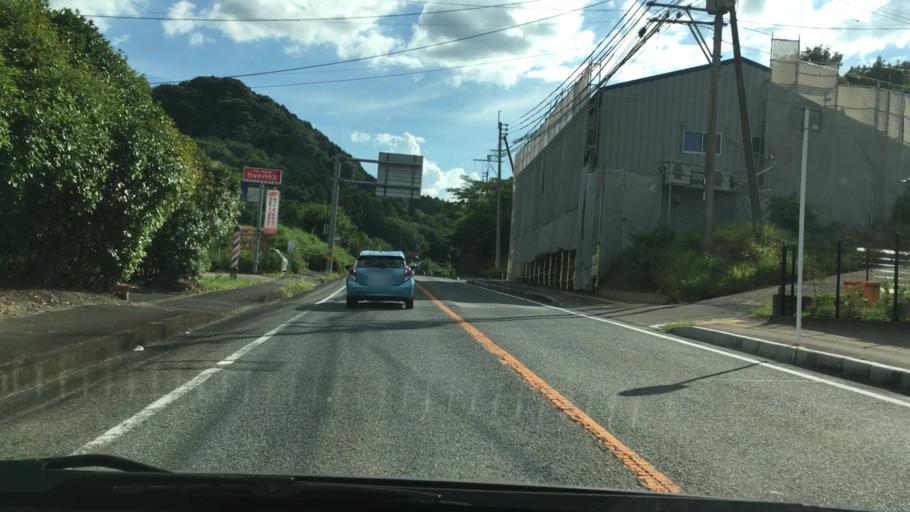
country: JP
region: Saga Prefecture
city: Imaricho-ko
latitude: 33.1889
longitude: 129.8602
